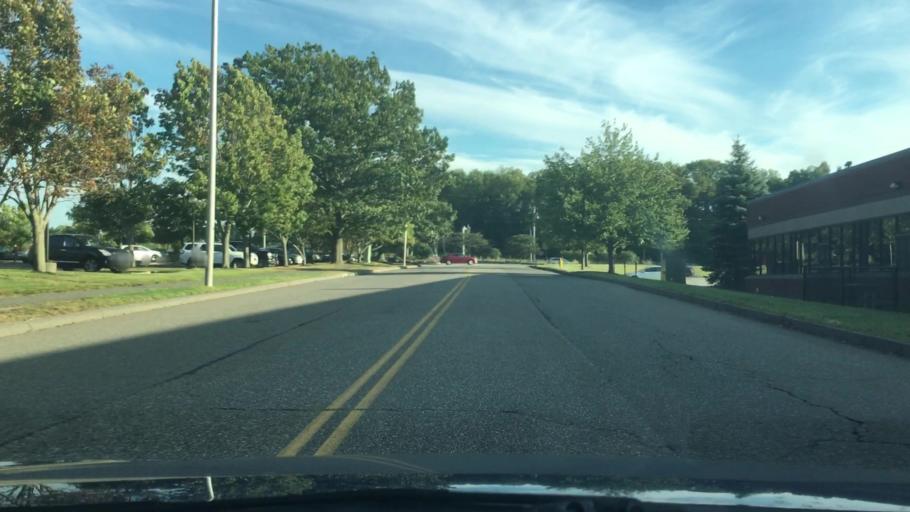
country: US
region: Massachusetts
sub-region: Worcester County
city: Westborough
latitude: 42.2900
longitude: -71.5738
